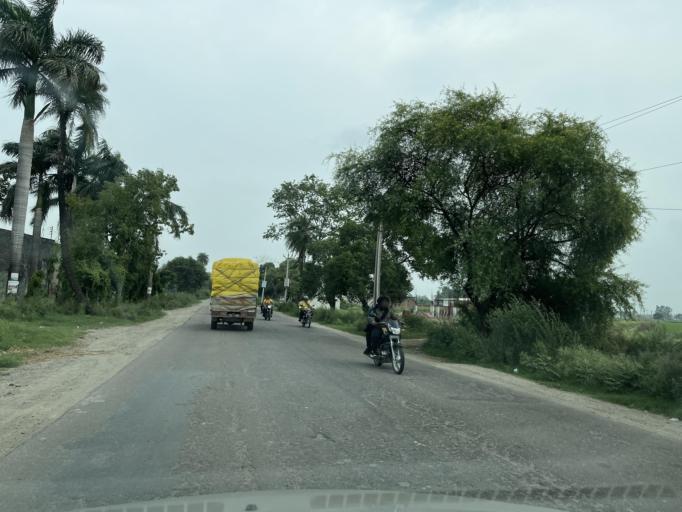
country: IN
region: Uttar Pradesh
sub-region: Rampur
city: Bilaspur
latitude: 29.0353
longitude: 79.2569
